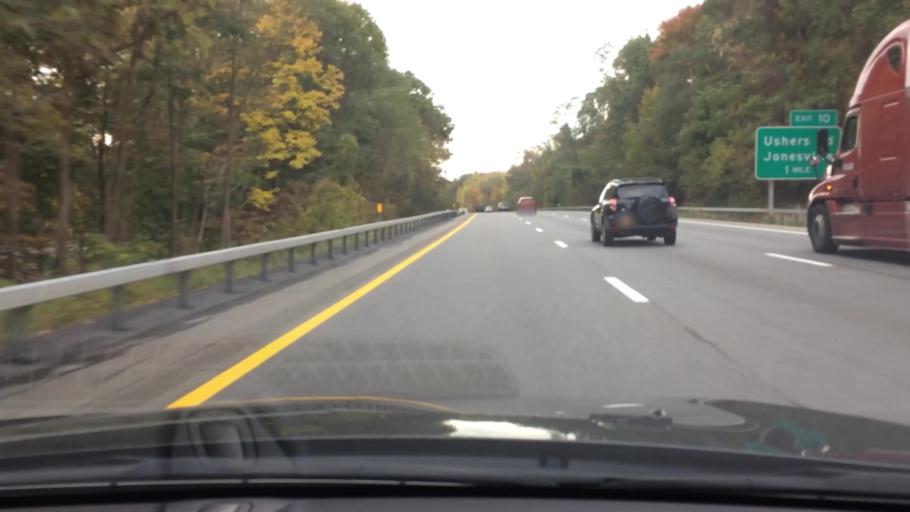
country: US
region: New York
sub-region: Saratoga County
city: Country Knolls
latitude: 42.9224
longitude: -73.8015
